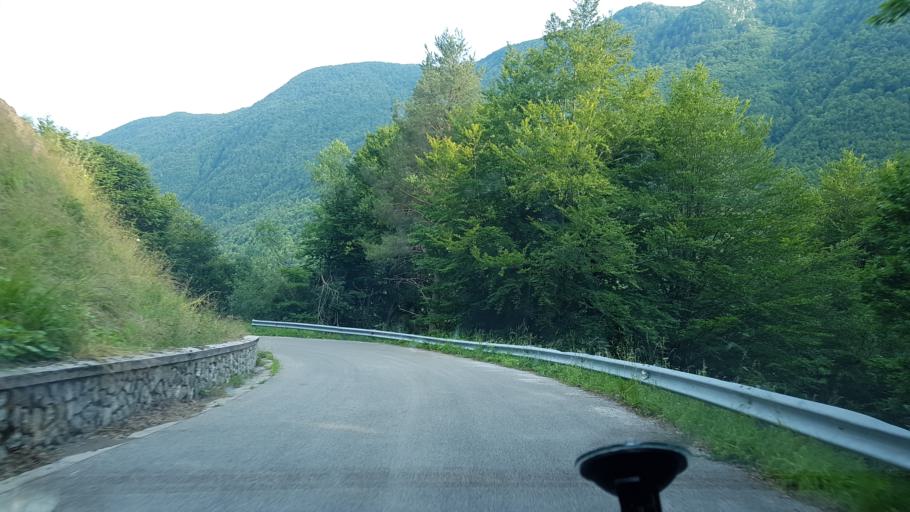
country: IT
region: Friuli Venezia Giulia
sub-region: Provincia di Udine
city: Prato
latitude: 46.3320
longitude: 13.3397
